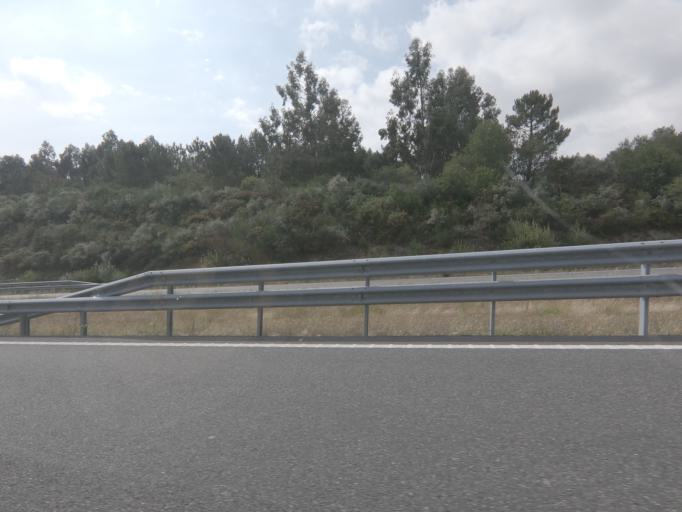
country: ES
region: Galicia
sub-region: Provincia de Ourense
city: Melon
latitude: 42.2146
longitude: -8.2592
